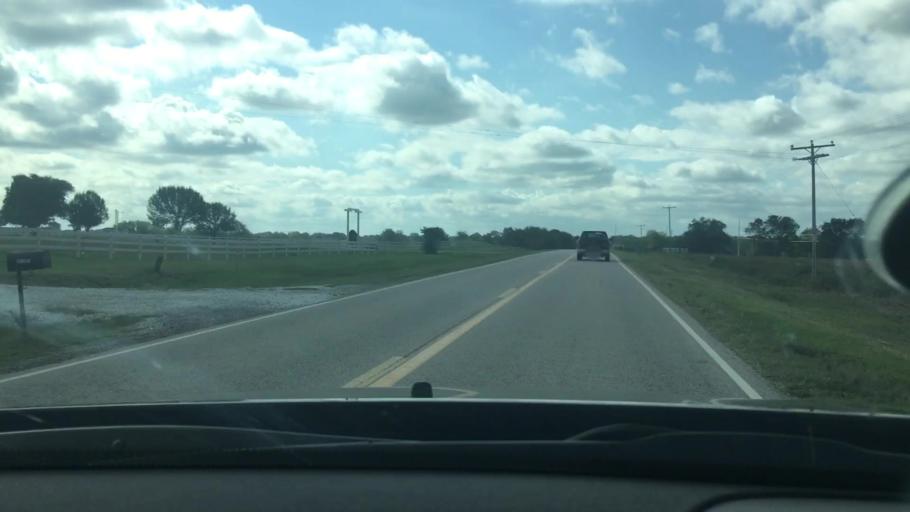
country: US
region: Oklahoma
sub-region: Pontotoc County
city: Ada
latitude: 34.7137
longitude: -96.6349
